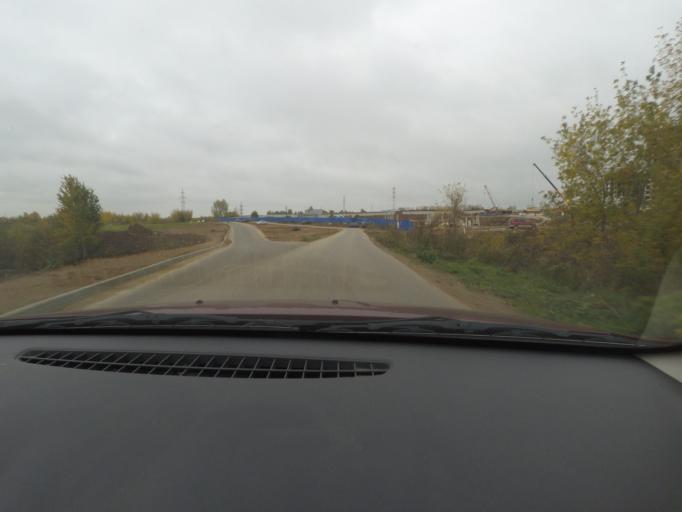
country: RU
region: Nizjnij Novgorod
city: Afonino
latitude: 56.2772
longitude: 44.0526
